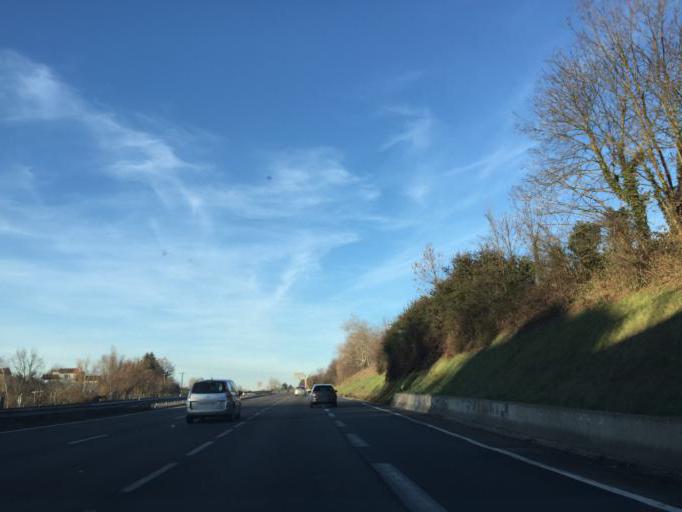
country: FR
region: Rhone-Alpes
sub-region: Departement de la Loire
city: La Fouillouse
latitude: 45.5103
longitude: 4.3018
